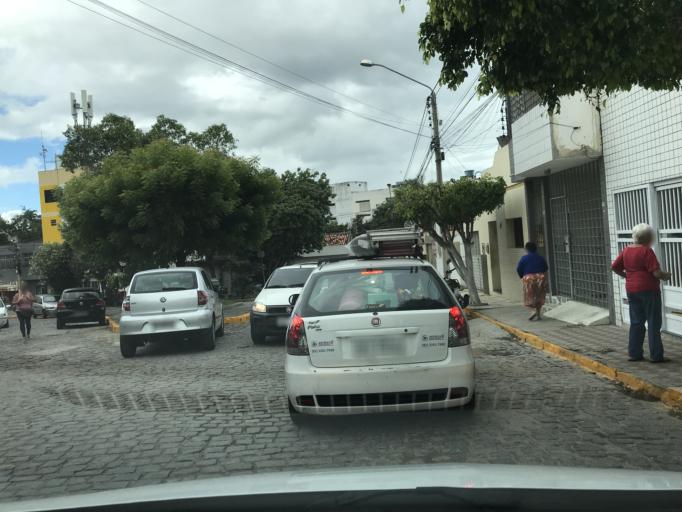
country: BR
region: Pernambuco
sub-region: Caruaru
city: Caruaru
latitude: -8.2893
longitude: -35.9754
